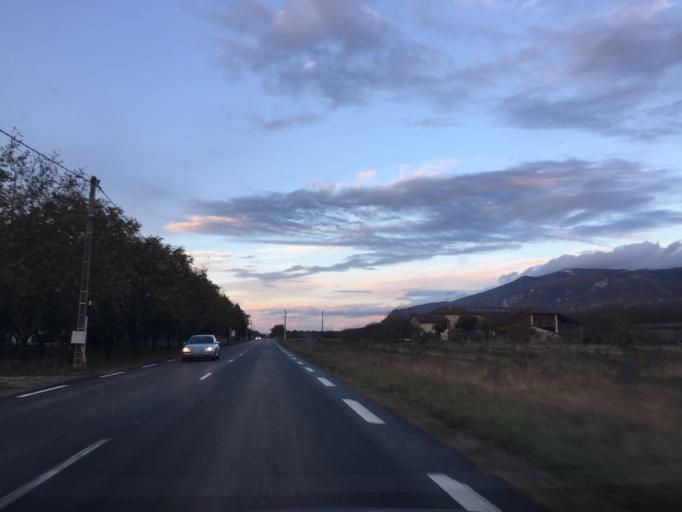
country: FR
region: Rhone-Alpes
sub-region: Departement de l'Isere
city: Saint-Just-de-Claix
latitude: 45.0928
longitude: 5.3017
